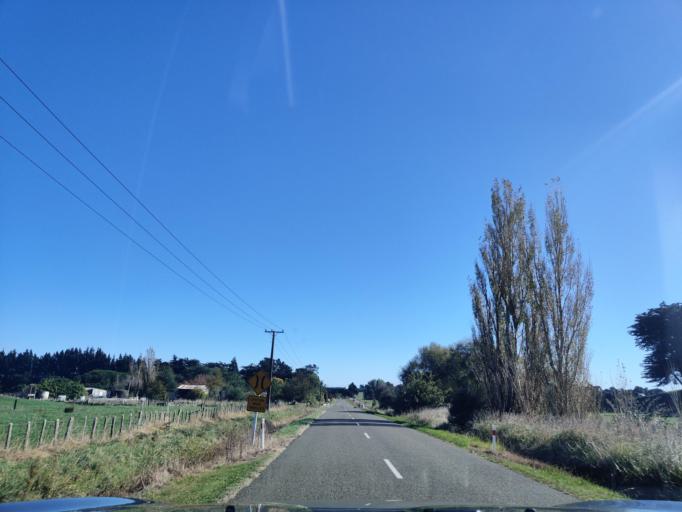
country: NZ
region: Manawatu-Wanganui
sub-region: Palmerston North City
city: Palmerston North
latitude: -40.2395
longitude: 175.6645
